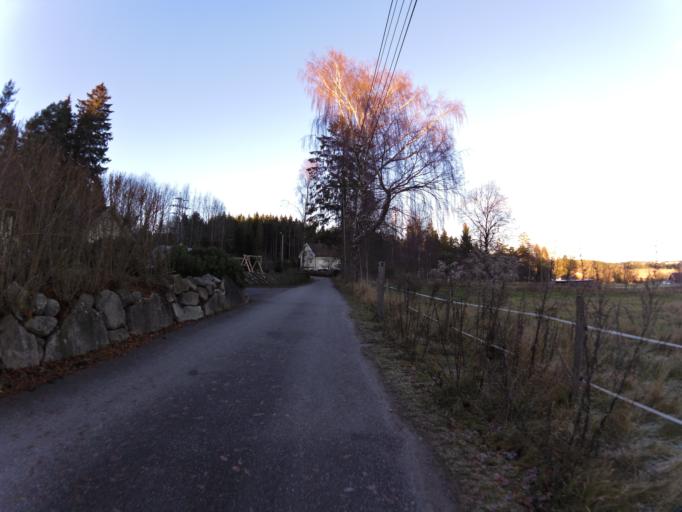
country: NO
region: Ostfold
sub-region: Fredrikstad
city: Fredrikstad
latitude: 59.2431
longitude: 10.9641
